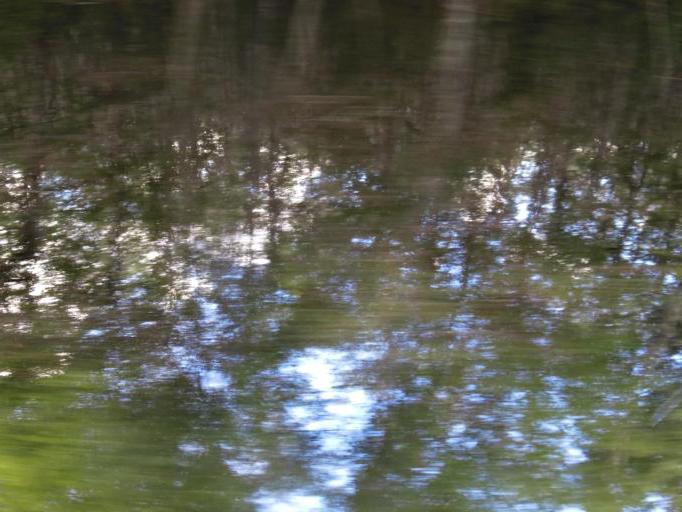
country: US
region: Georgia
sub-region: Echols County
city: Statenville
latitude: 30.7498
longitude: -83.1090
